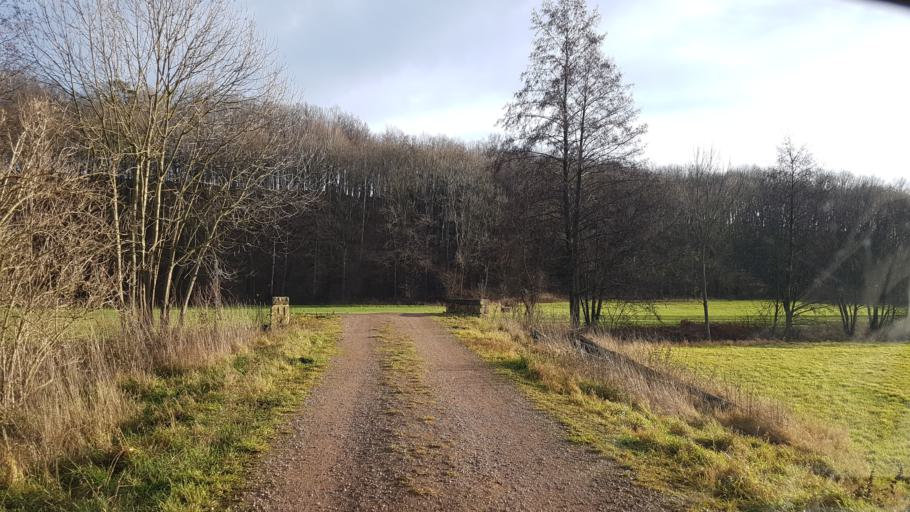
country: DE
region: Saxony
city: Ostrau
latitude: 51.1817
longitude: 13.1671
